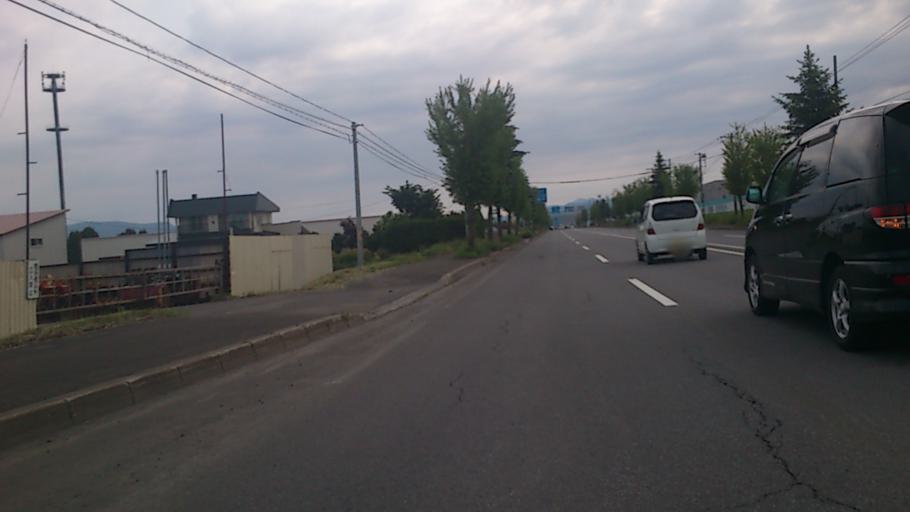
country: JP
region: Hokkaido
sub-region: Asahikawa-shi
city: Asahikawa
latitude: 43.8422
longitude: 142.4846
